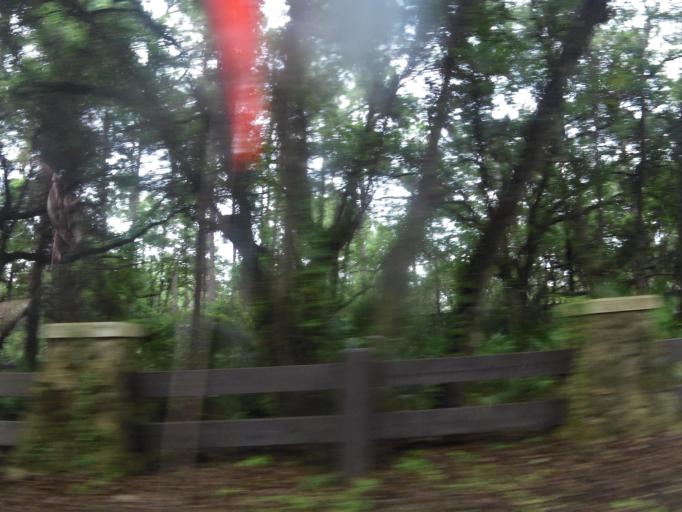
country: US
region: Florida
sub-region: Saint Johns County
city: Ponte Vedra Beach
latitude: 30.2517
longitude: -81.4363
